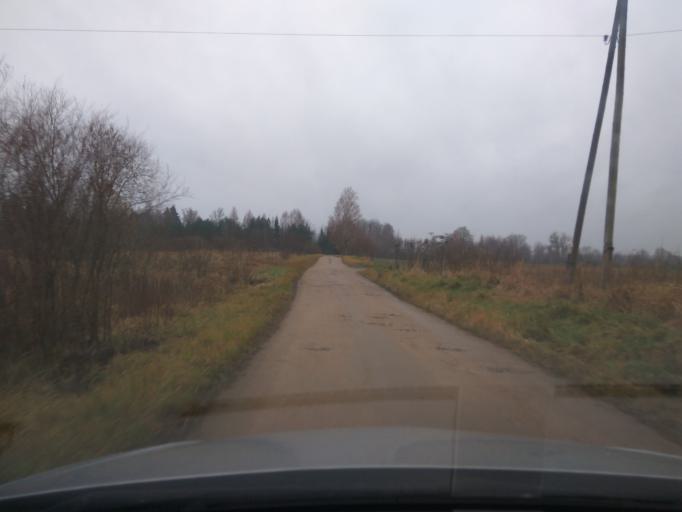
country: LV
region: Kuldigas Rajons
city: Kuldiga
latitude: 56.9342
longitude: 22.0102
